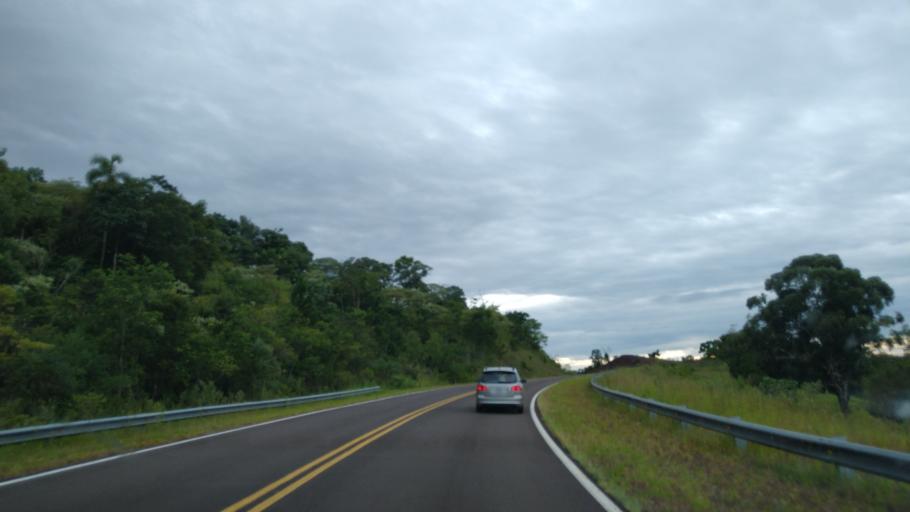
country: AR
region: Misiones
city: Bernardo de Irigoyen
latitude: -26.3842
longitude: -53.7948
